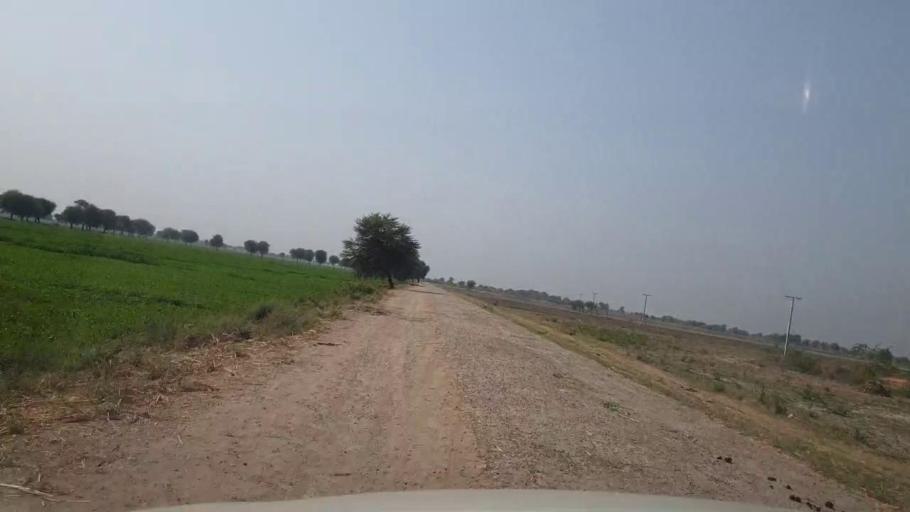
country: PK
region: Sindh
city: Chor
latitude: 25.4684
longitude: 69.6749
